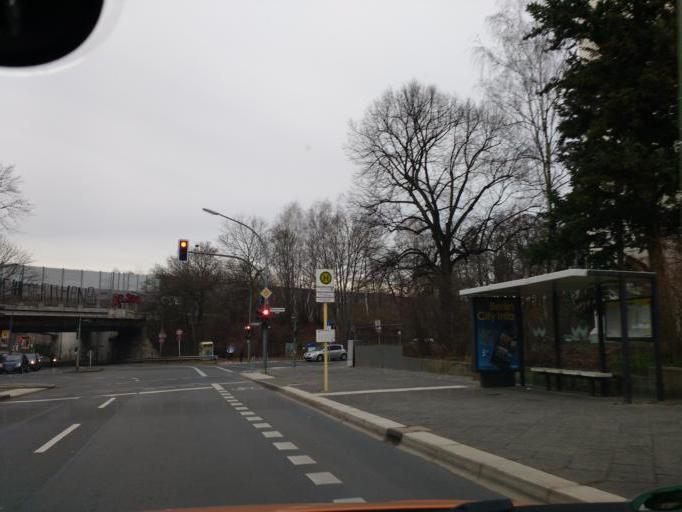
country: DE
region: Berlin
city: Schoneberg Bezirk
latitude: 52.4566
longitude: 13.3598
